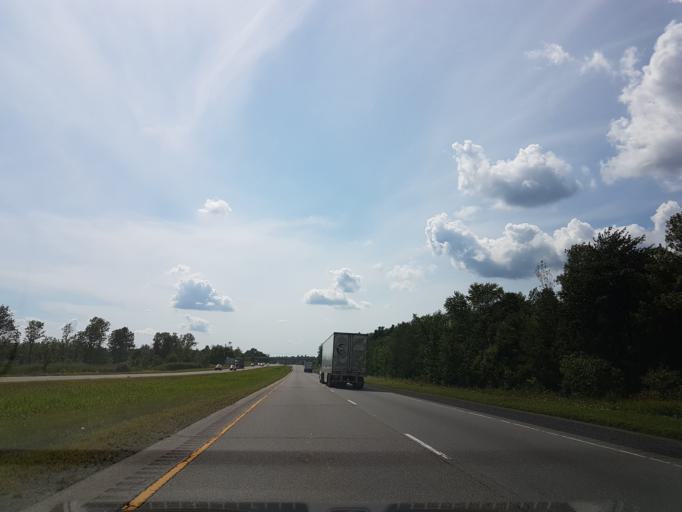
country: CA
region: Ontario
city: Prescott
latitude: 44.7184
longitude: -75.5357
